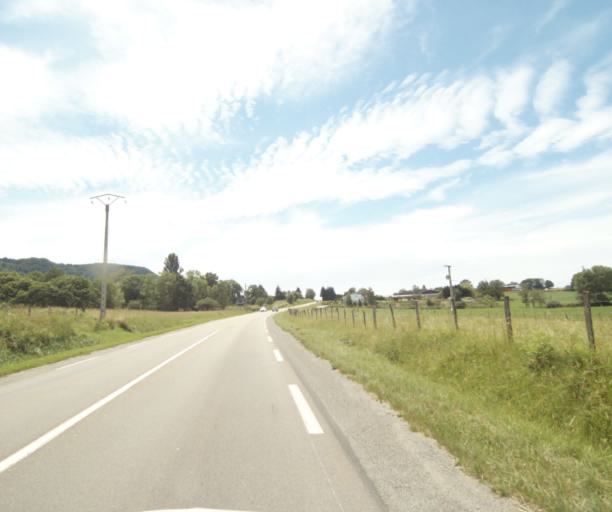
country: FR
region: Rhone-Alpes
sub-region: Departement de la Haute-Savoie
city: Allinges
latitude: 46.3383
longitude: 6.4571
